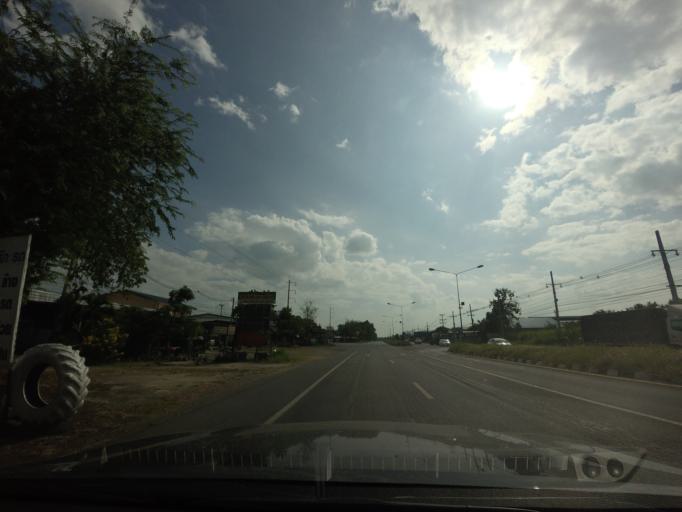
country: TH
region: Lop Buri
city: Chai Badan
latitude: 15.1865
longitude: 101.0764
